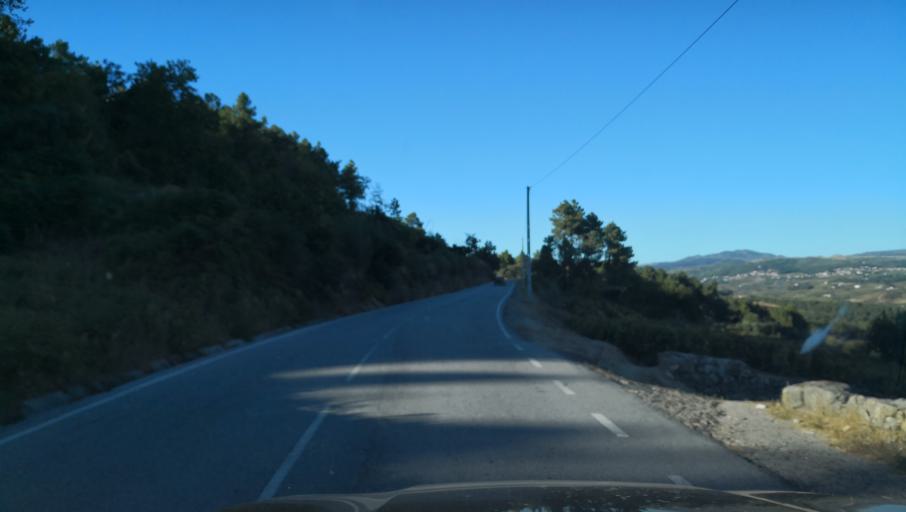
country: PT
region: Vila Real
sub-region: Sabrosa
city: Sabrosa
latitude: 41.2777
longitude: -7.5688
